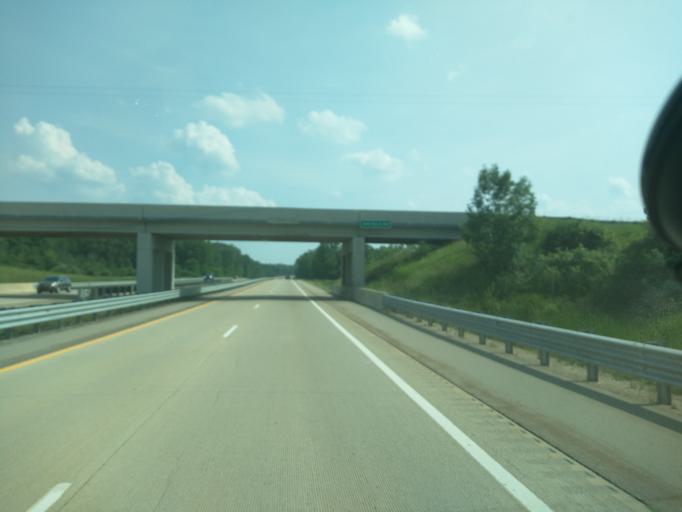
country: US
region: Michigan
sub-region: Jackson County
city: Jackson
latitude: 42.3280
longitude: -84.4290
